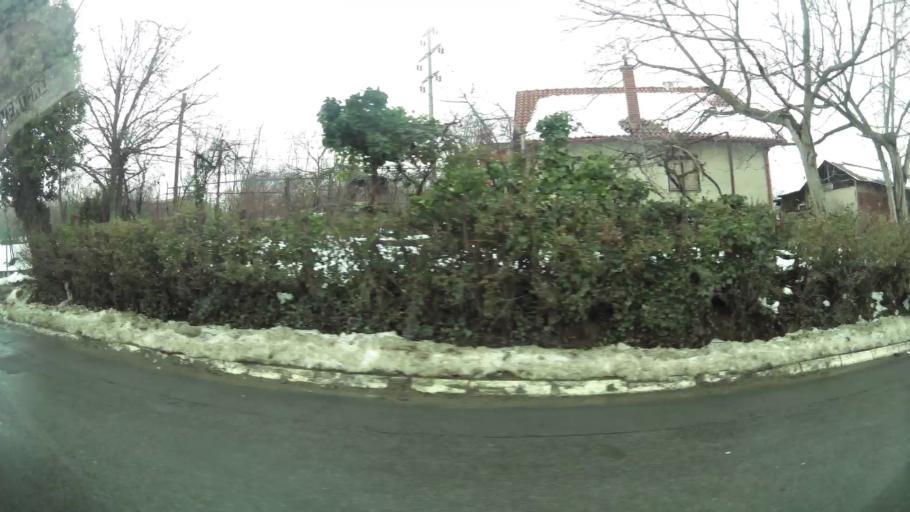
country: RS
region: Central Serbia
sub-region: Belgrade
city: Zvezdara
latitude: 44.7684
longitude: 20.5175
